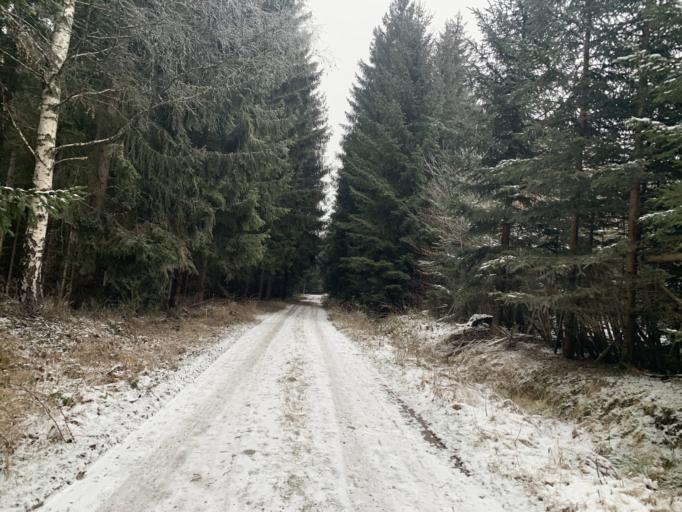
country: CZ
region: Central Bohemia
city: Rozmital pod Tremsinem
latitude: 49.5820
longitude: 13.8344
